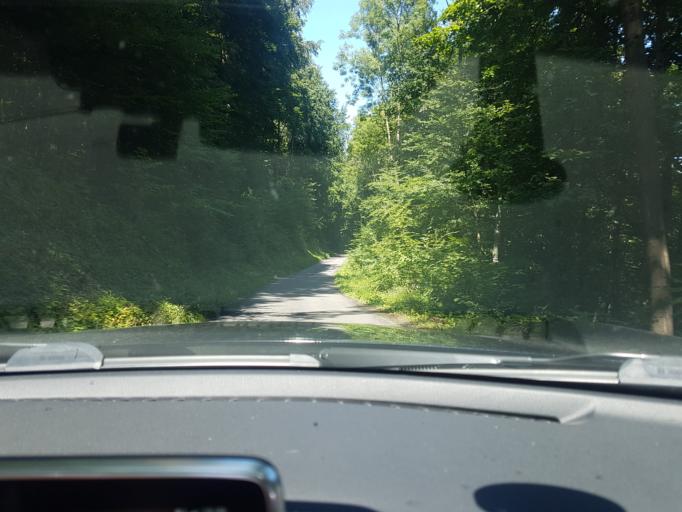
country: DE
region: Baden-Wuerttemberg
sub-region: Karlsruhe Region
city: Neckarzimmern
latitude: 49.3164
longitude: 9.1464
